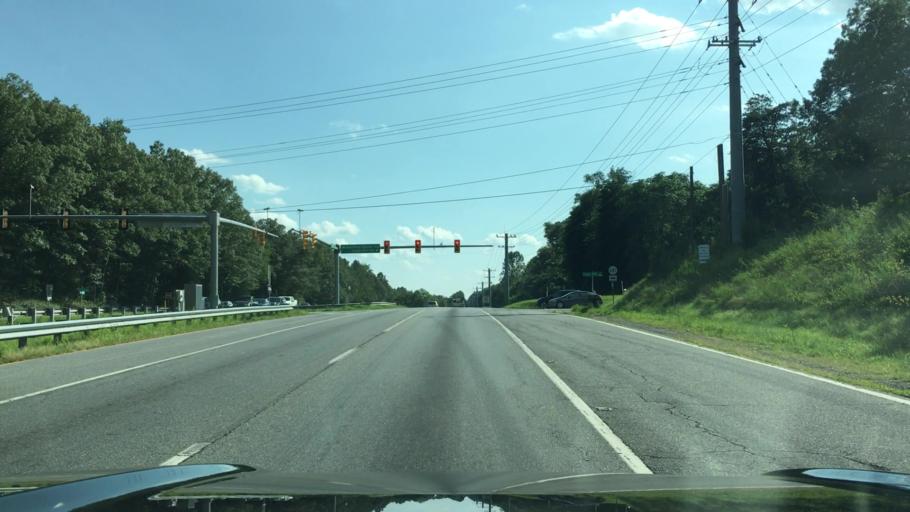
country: US
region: Virginia
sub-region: Greene County
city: Ruckersville
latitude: 38.1859
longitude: -78.4008
